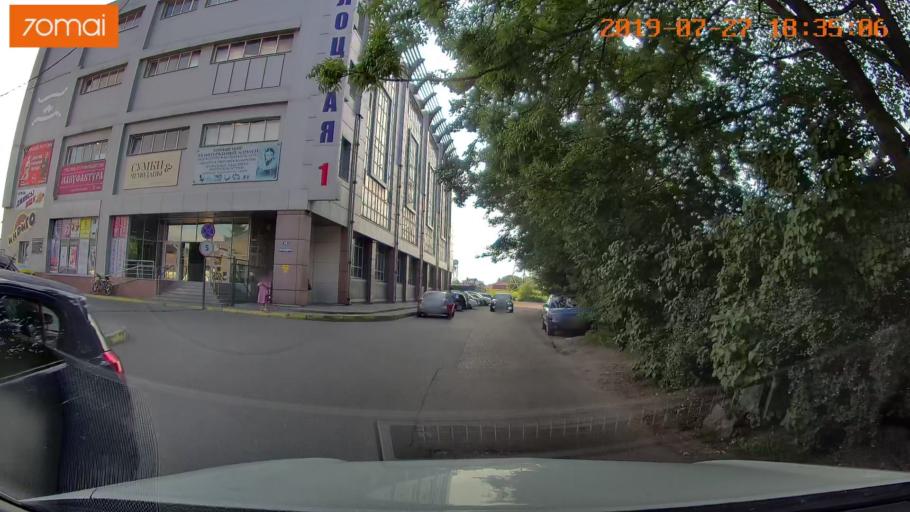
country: RU
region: Kaliningrad
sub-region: Gorod Kaliningrad
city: Kaliningrad
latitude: 54.7032
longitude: 20.4995
